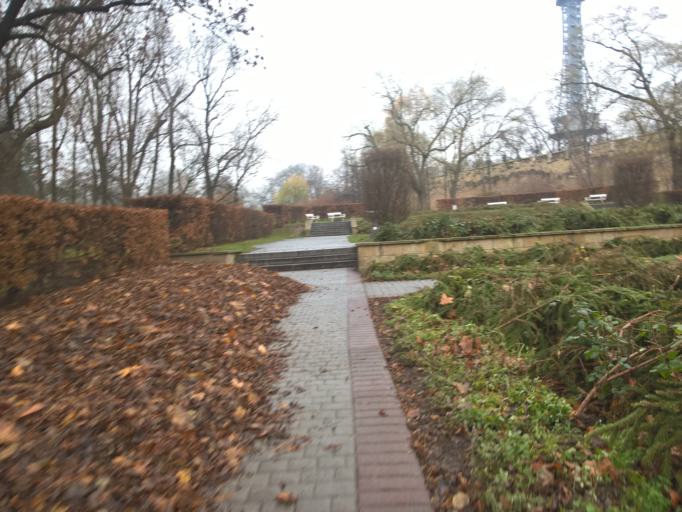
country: CZ
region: Praha
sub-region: Praha 1
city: Mala Strana
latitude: 50.0825
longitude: 14.3963
